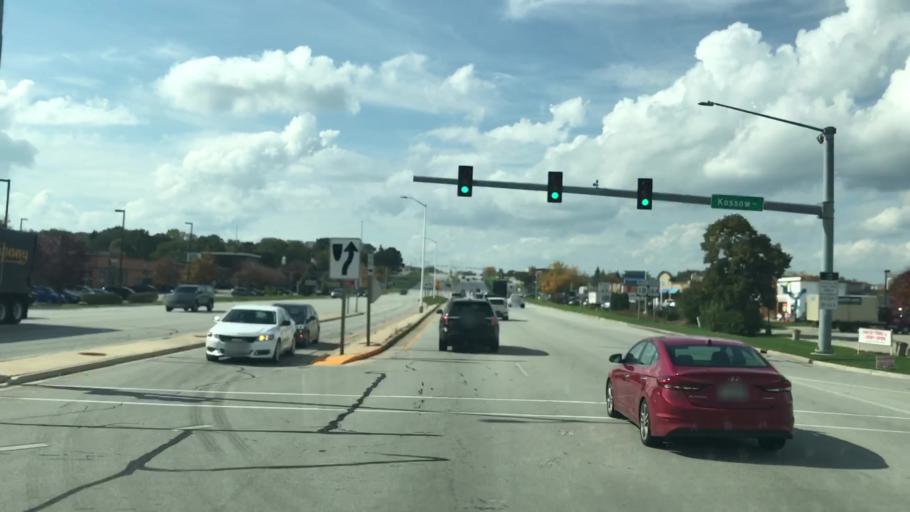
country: US
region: Wisconsin
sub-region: Waukesha County
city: Waukesha
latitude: 43.0320
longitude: -88.1779
